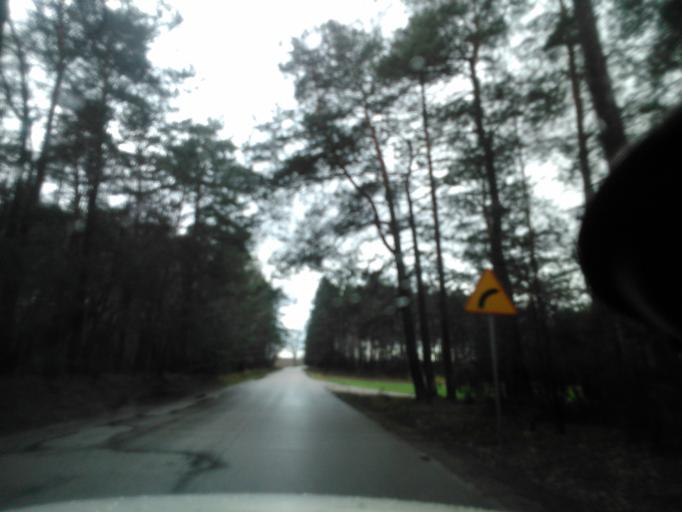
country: PL
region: Warmian-Masurian Voivodeship
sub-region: Powiat dzialdowski
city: Lidzbark
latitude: 53.2804
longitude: 19.8450
